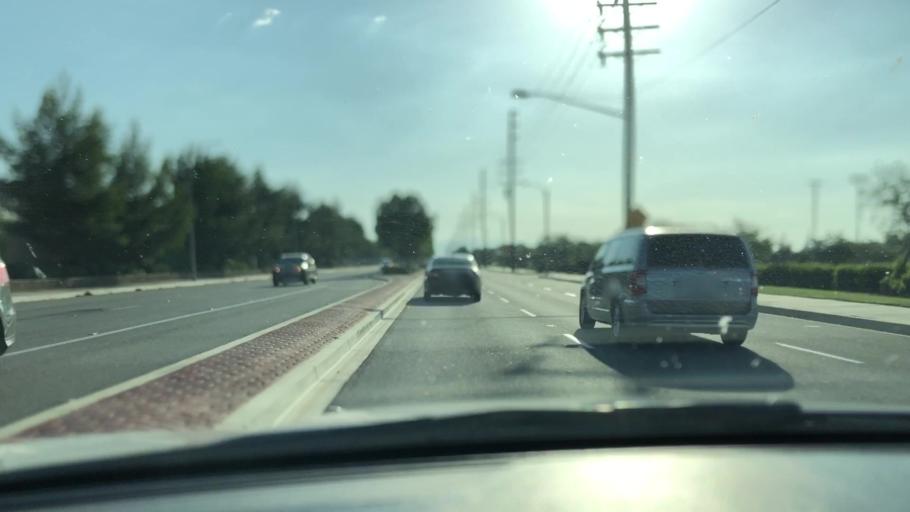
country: US
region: California
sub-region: Los Angeles County
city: Quartz Hill
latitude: 34.6749
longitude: -118.1885
